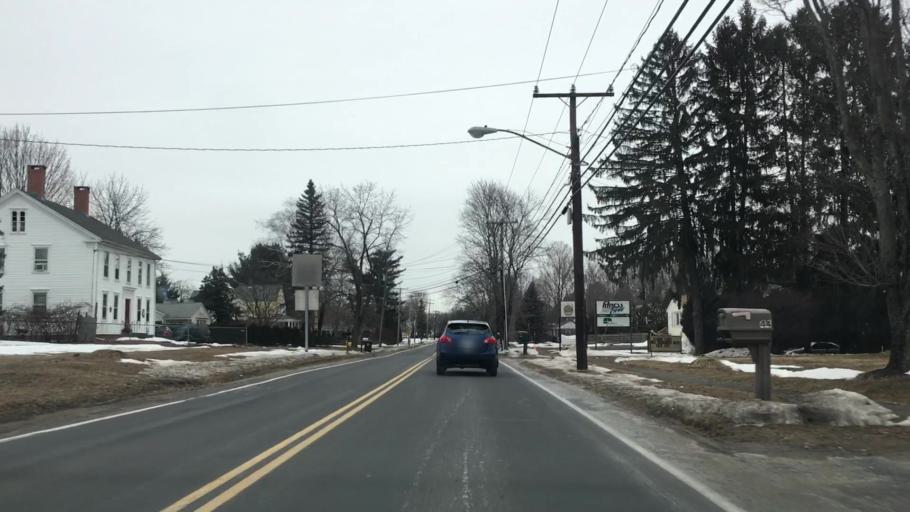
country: US
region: Massachusetts
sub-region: Hampden County
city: Agawam
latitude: 42.0685
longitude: -72.6787
